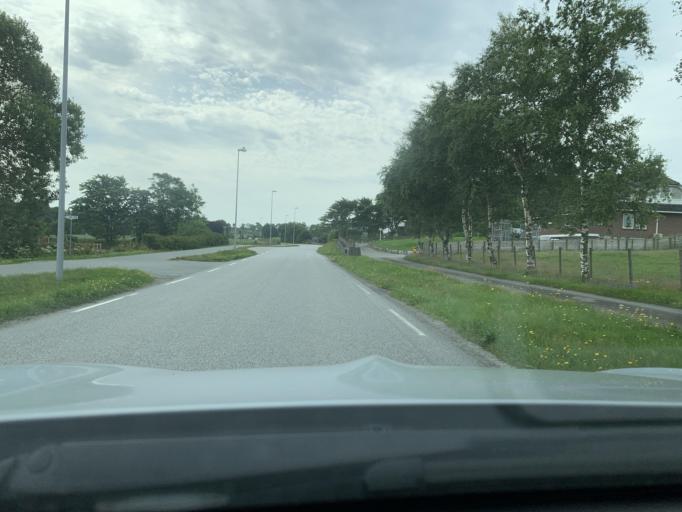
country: NO
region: Rogaland
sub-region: Time
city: Bryne
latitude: 58.7607
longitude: 5.7096
